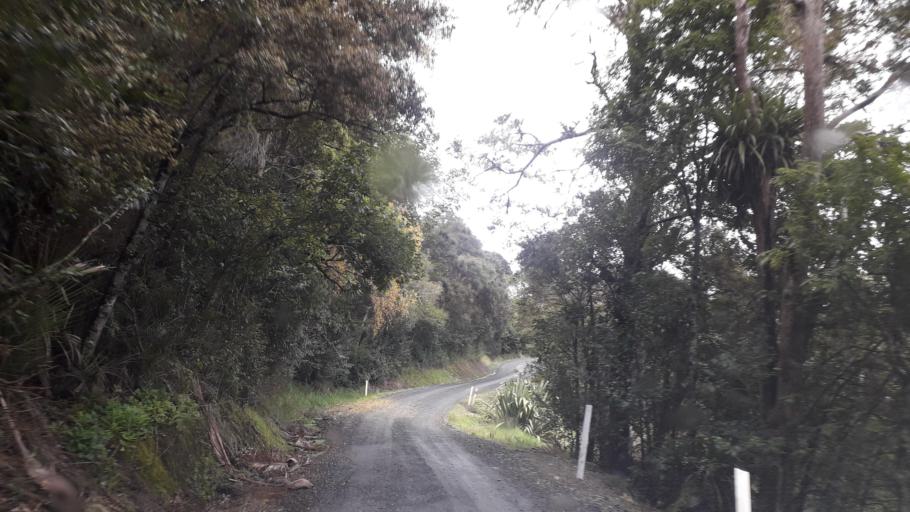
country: NZ
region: Northland
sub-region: Far North District
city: Waimate North
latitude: -35.3079
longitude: 173.5639
